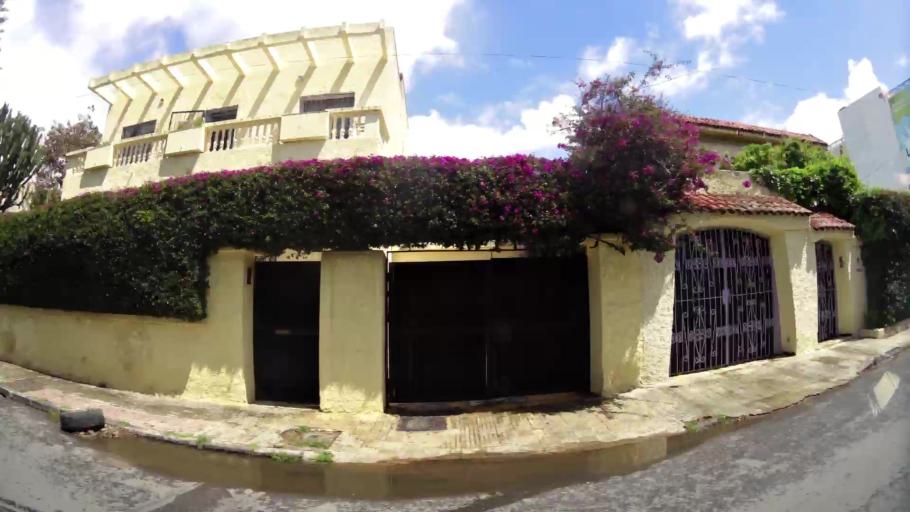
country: MA
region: Grand Casablanca
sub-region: Casablanca
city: Casablanca
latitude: 33.5701
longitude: -7.6416
